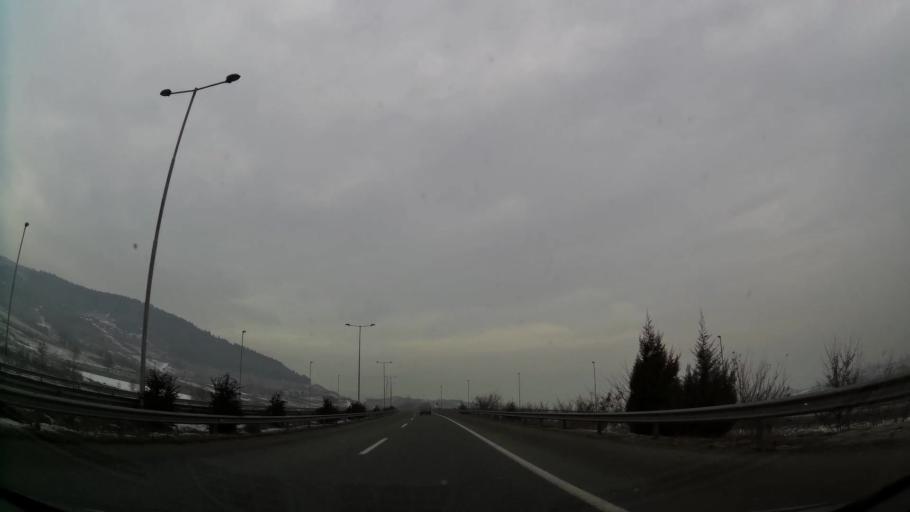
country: MK
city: Kondovo
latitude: 42.0395
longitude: 21.3366
